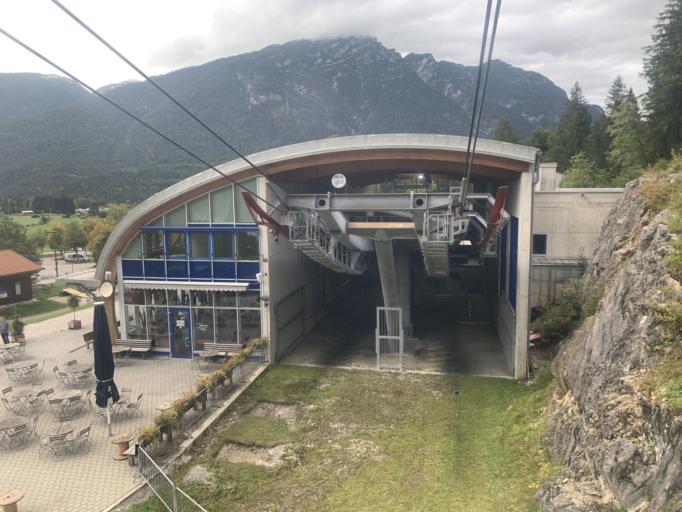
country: DE
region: Bavaria
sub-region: Upper Bavaria
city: Garmisch-Partenkirchen
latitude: 47.4712
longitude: 11.0638
